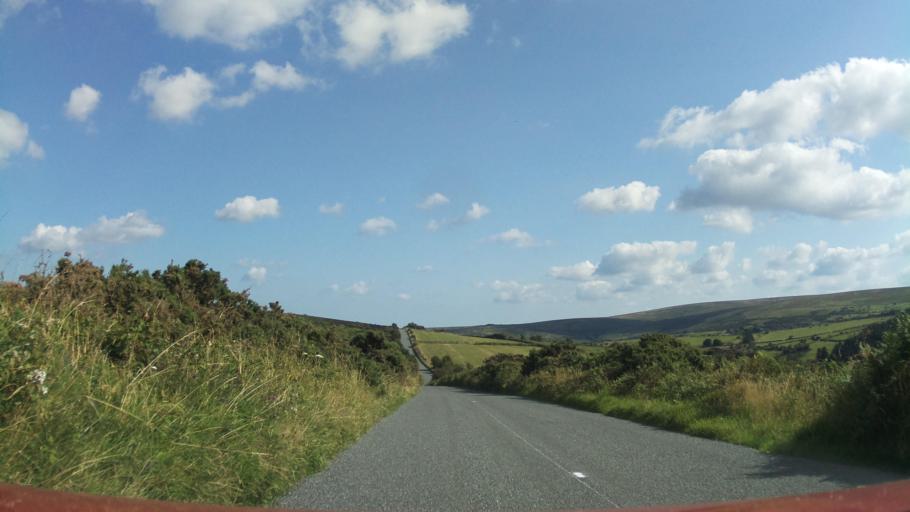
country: GB
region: England
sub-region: Devon
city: South Brent
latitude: 50.5526
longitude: -3.9066
